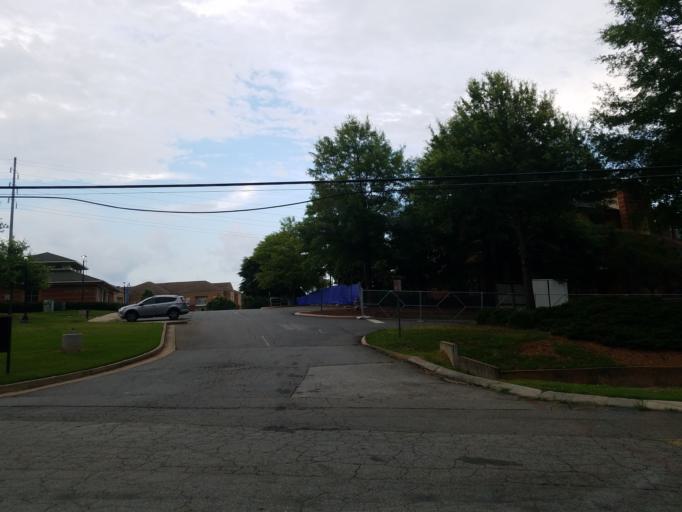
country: US
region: Georgia
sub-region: Cobb County
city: Fair Oaks
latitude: 33.9379
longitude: -84.5182
